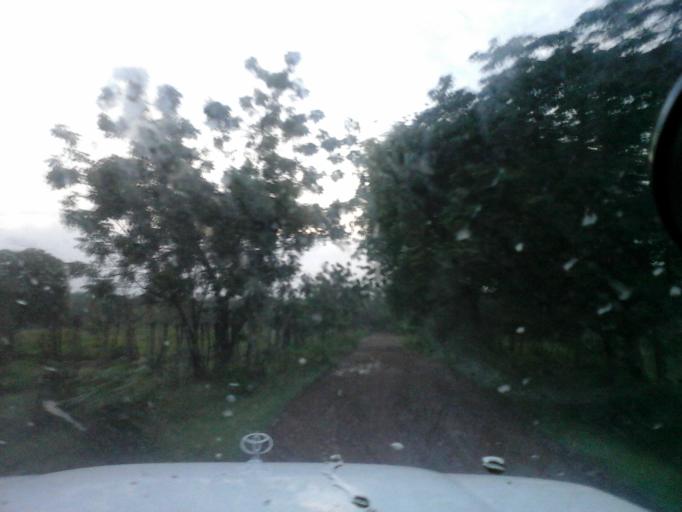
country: CO
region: Cesar
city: Agustin Codazzi
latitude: 10.1617
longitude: -73.2011
